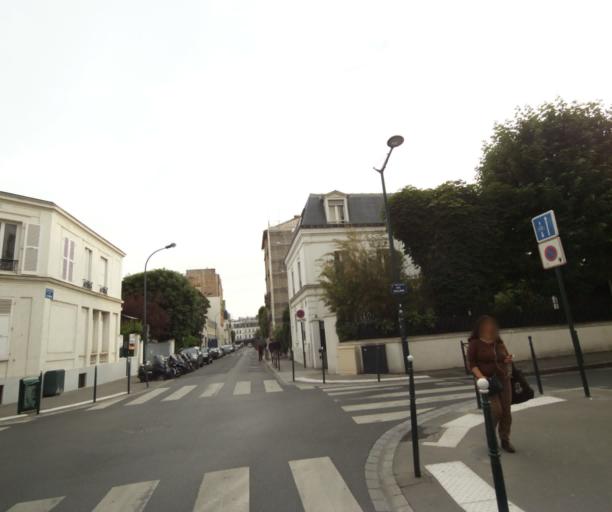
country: FR
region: Ile-de-France
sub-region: Departement des Hauts-de-Seine
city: Asnieres-sur-Seine
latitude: 48.9073
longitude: 2.2885
